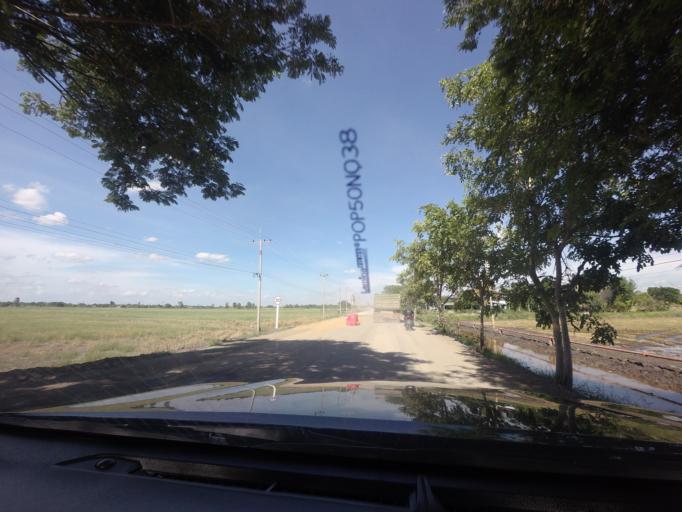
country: TH
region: Suphan Buri
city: Song Phi Nong
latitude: 14.1780
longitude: 100.0362
